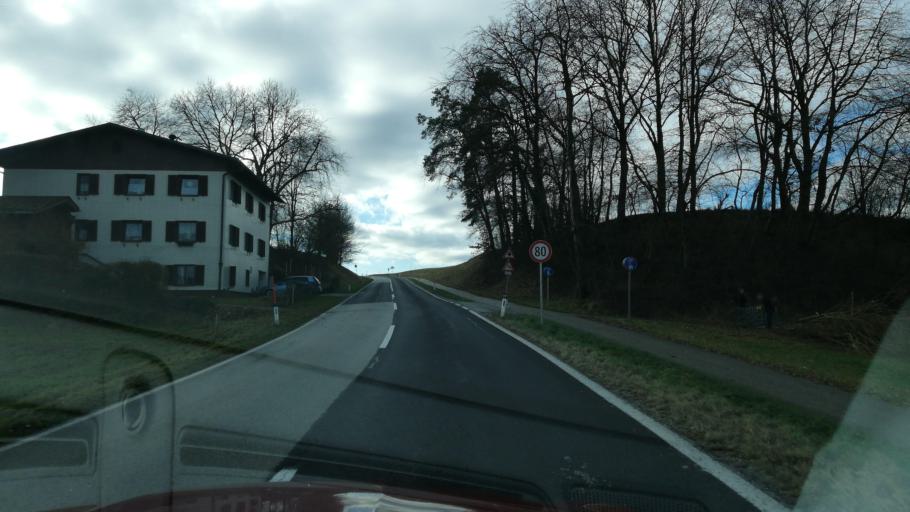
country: AT
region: Upper Austria
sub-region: Politischer Bezirk Braunau am Inn
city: Braunau am Inn
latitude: 48.1992
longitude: 13.0910
